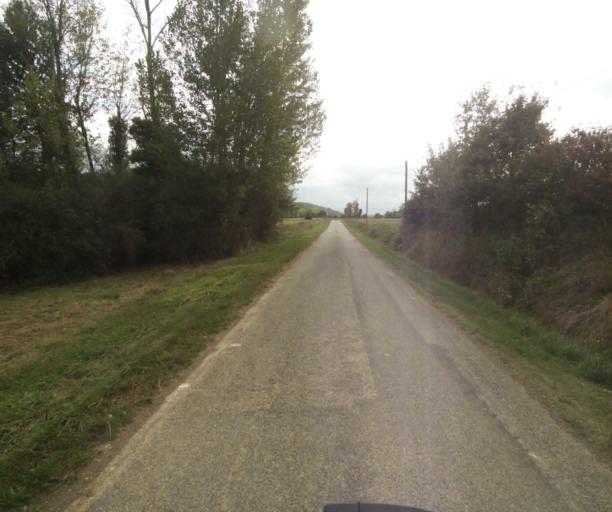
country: FR
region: Midi-Pyrenees
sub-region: Departement de la Haute-Garonne
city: Launac
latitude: 43.8427
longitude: 1.1110
